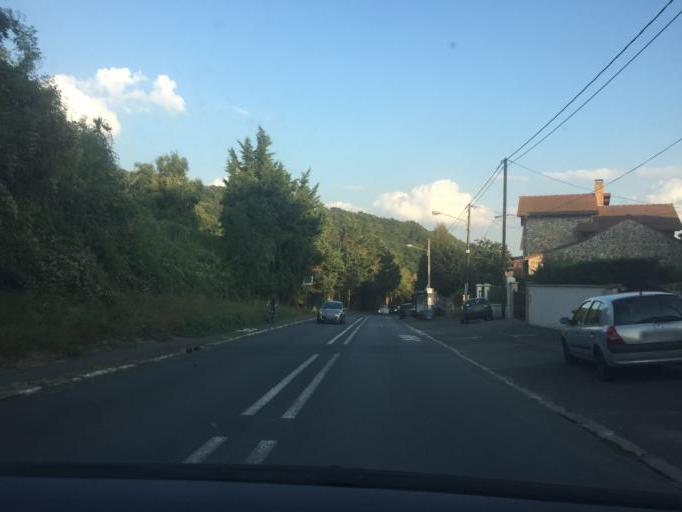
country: FR
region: Ile-de-France
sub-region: Departement de l'Essonne
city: Orsay
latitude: 48.7116
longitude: 2.1843
